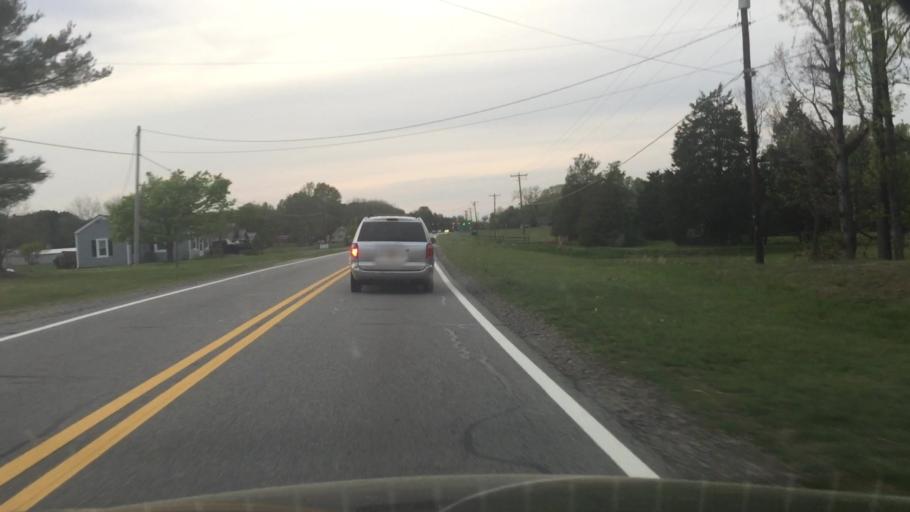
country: US
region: North Carolina
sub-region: Rockingham County
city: Reidsville
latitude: 36.3087
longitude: -79.6270
